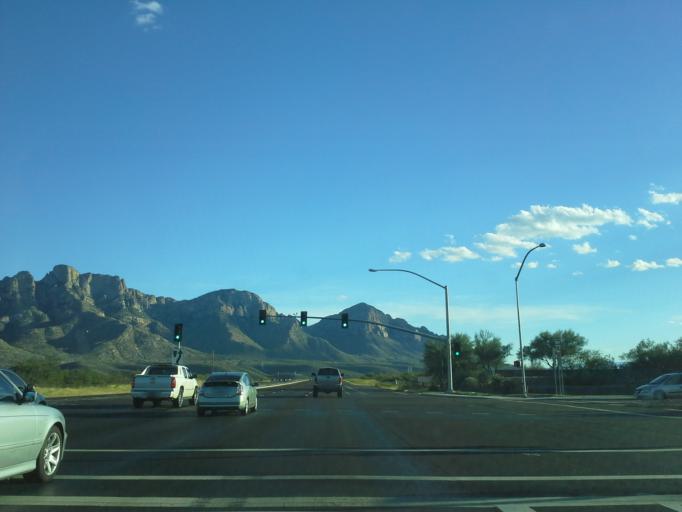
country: US
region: Arizona
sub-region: Pima County
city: Oro Valley
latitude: 32.4386
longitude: -110.9345
